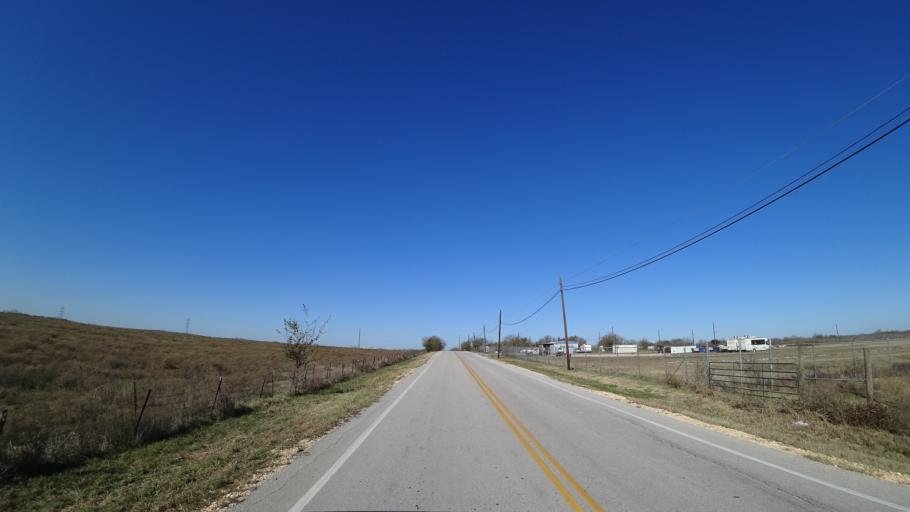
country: US
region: Texas
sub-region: Travis County
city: Garfield
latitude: 30.1141
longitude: -97.6515
